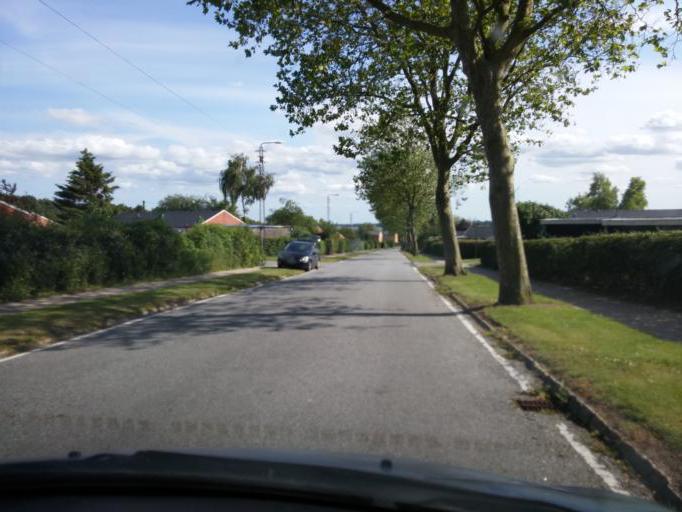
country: DK
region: South Denmark
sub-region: Kerteminde Kommune
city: Munkebo
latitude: 55.4632
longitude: 10.5562
